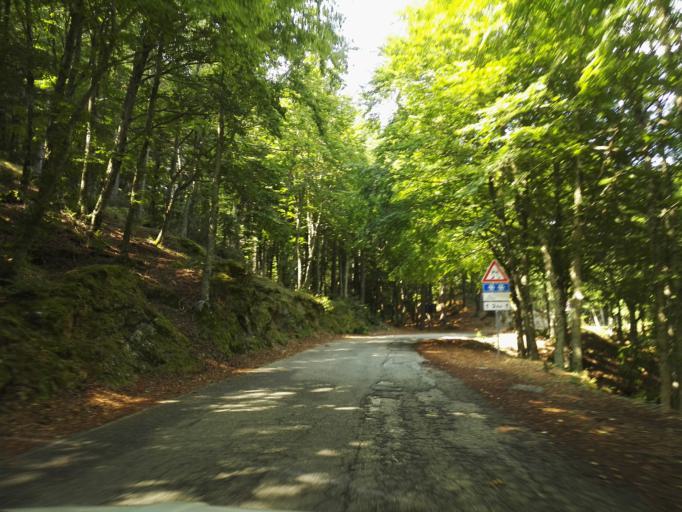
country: IT
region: Calabria
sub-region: Provincia di Vibo-Valentia
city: Nardodipace
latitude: 38.4886
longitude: 16.3776
